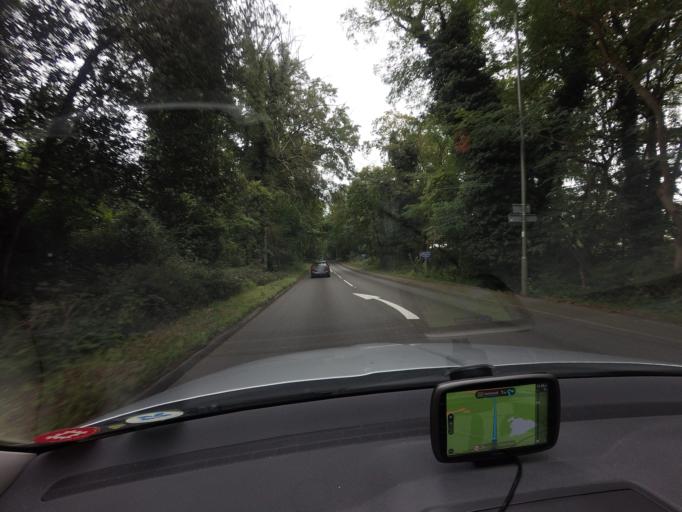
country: GB
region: England
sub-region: Surrey
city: Byfleet
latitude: 51.3387
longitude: -0.4503
